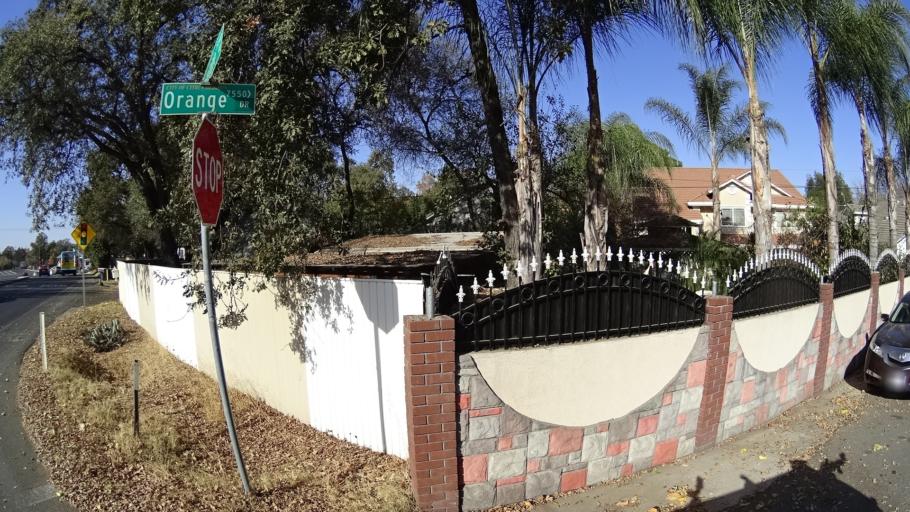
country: US
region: California
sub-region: Sacramento County
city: Citrus Heights
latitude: 38.7064
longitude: -121.2885
